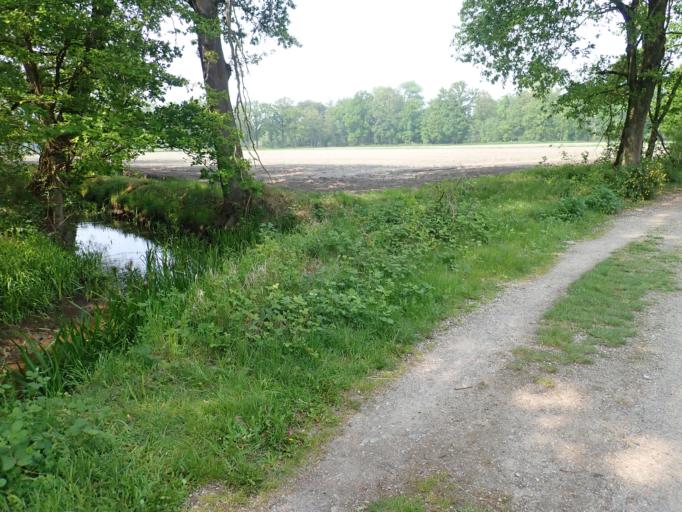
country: BE
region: Flanders
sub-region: Provincie Antwerpen
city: Oud-Turnhout
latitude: 51.3334
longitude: 4.9977
